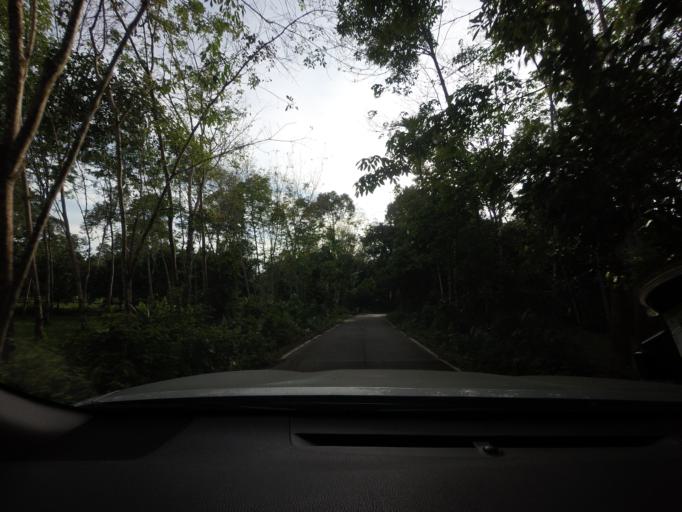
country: TH
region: Narathiwat
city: Ra-ngae
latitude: 6.3005
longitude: 101.7705
